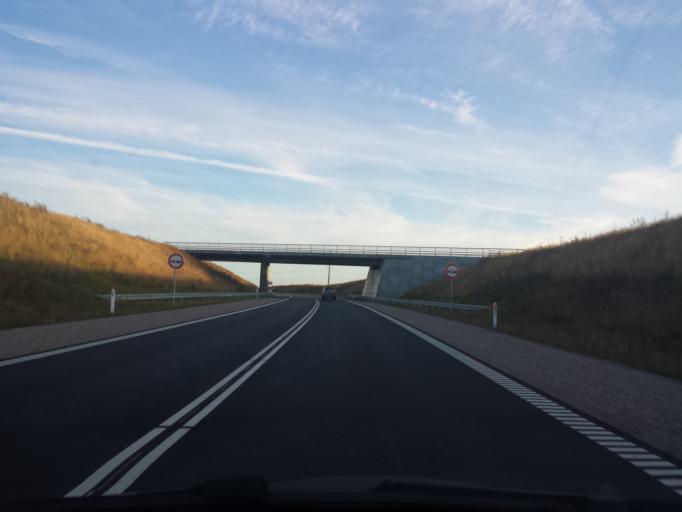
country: DK
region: Capital Region
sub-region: Egedal Kommune
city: Smorumnedre
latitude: 55.7327
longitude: 12.2827
